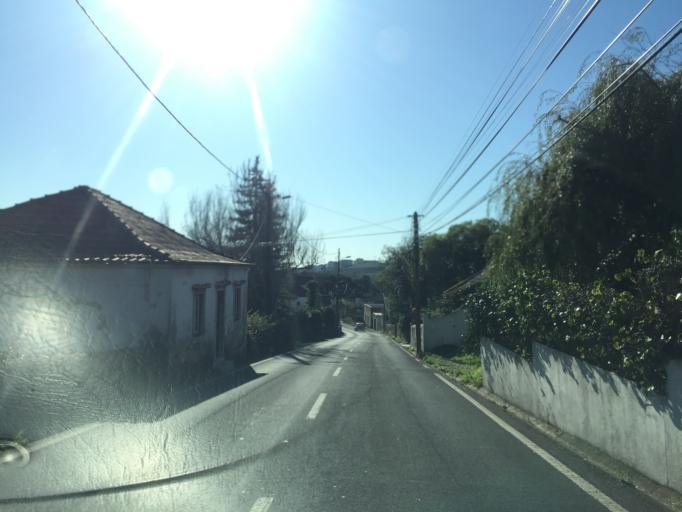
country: PT
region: Lisbon
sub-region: Sintra
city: Belas
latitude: 38.7855
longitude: -9.2649
